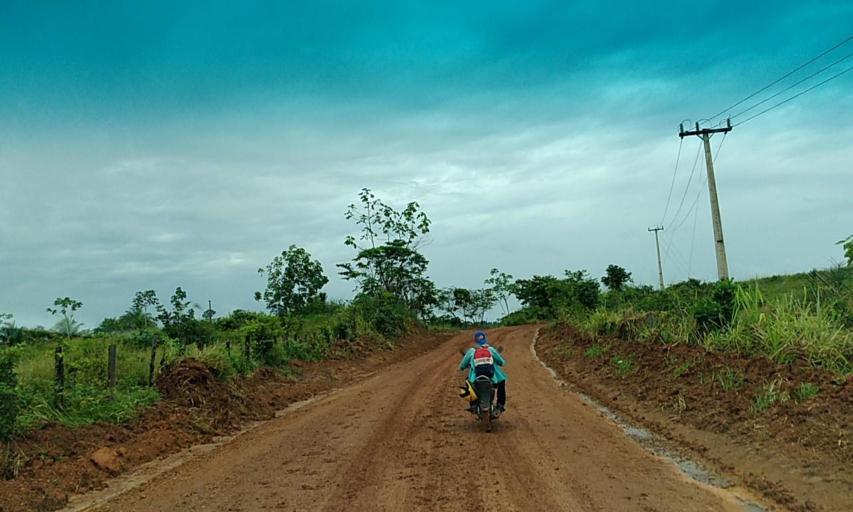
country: BR
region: Para
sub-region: Altamira
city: Altamira
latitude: -3.0899
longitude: -51.6341
